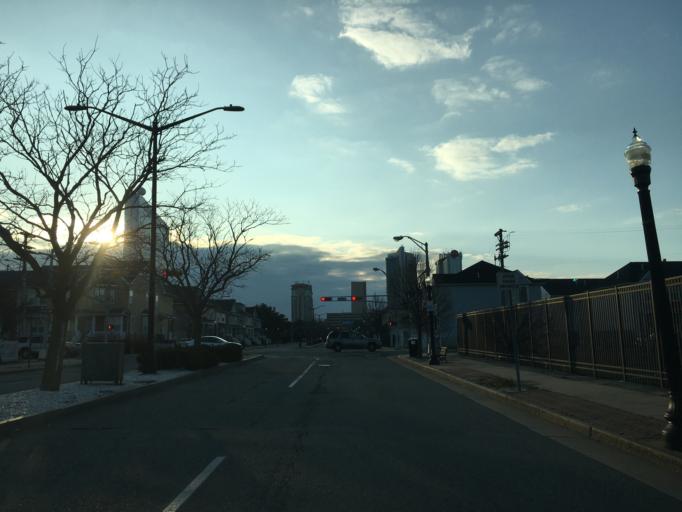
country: US
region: New Jersey
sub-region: Atlantic County
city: Atlantic City
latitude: 39.3684
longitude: -74.4227
